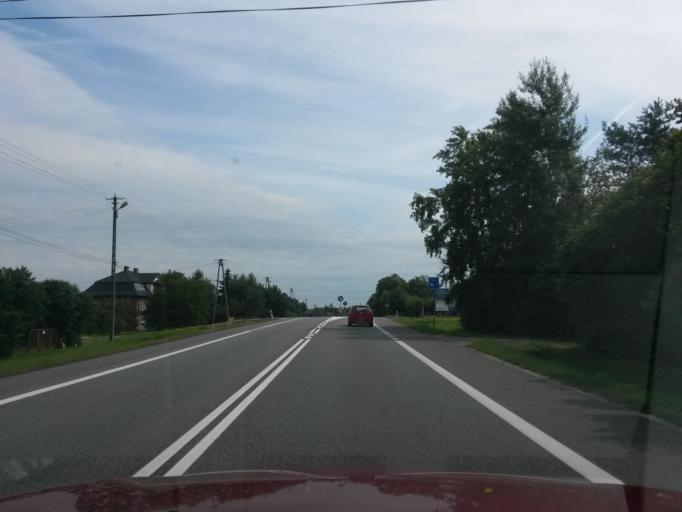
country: PL
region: Lesser Poland Voivodeship
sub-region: Powiat brzeski
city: Jasien
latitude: 49.9742
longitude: 20.5550
